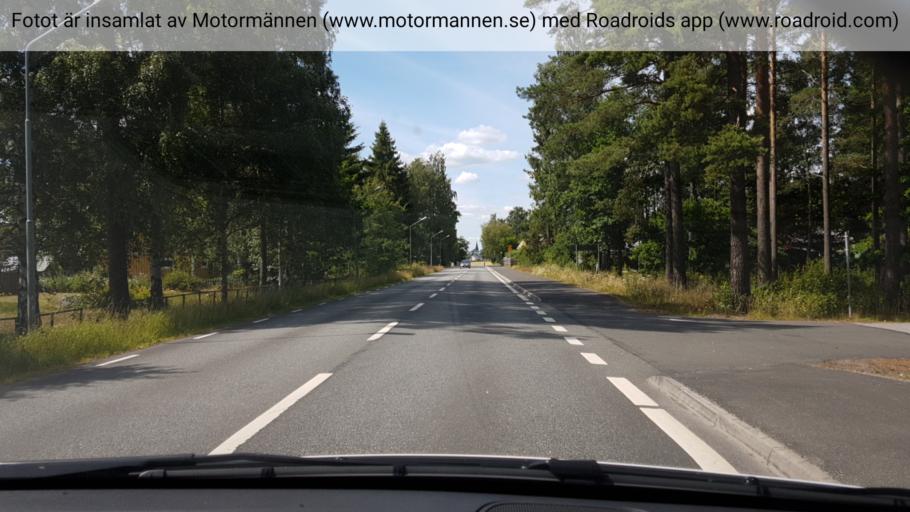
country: SE
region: Vaestra Goetaland
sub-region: Toreboda Kommun
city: Toereboda
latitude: 58.6081
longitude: 14.0339
